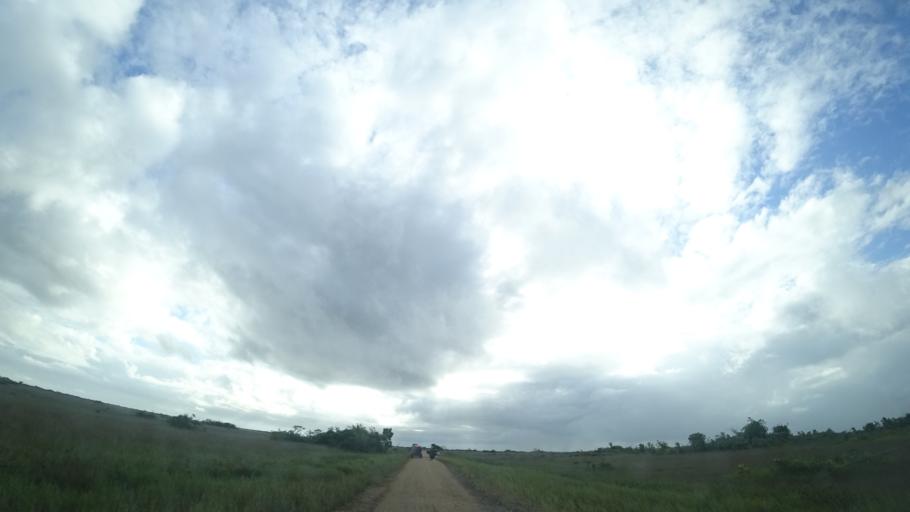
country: MZ
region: Sofala
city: Beira
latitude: -19.7009
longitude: 35.0262
